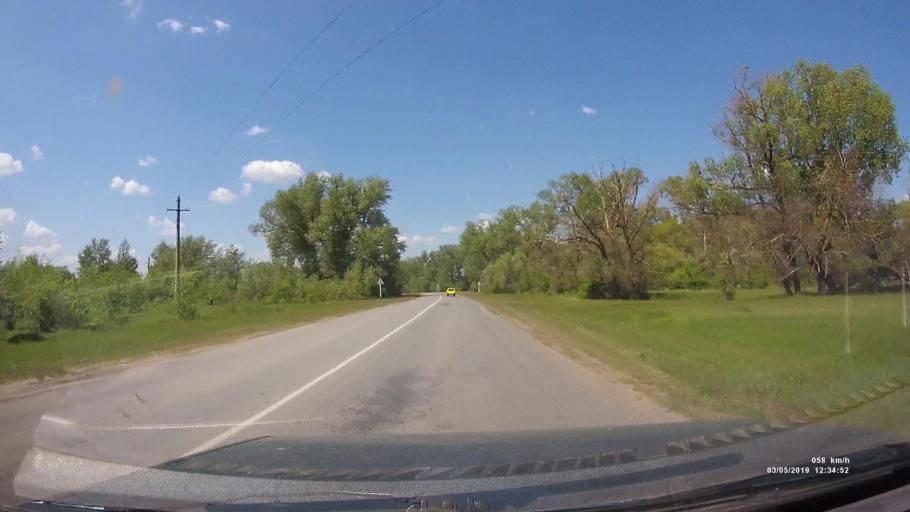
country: RU
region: Rostov
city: Semikarakorsk
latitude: 47.5234
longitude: 40.7648
